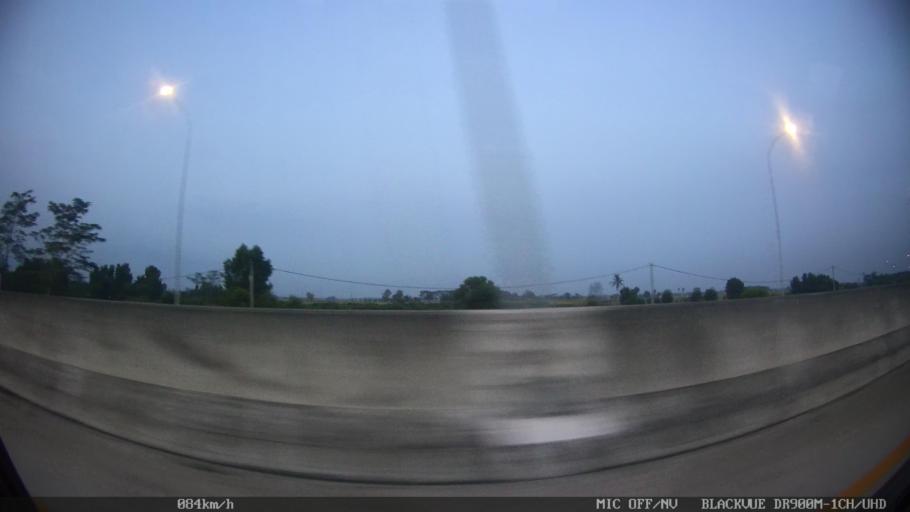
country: ID
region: Lampung
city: Sidorejo
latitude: -5.6054
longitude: 105.5557
